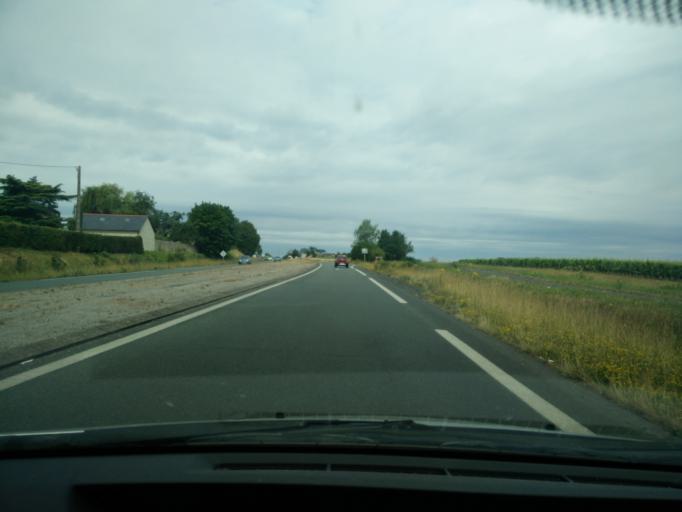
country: FR
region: Pays de la Loire
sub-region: Departement de Maine-et-Loire
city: Brissac-Quince
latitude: 47.3624
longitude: -0.4477
